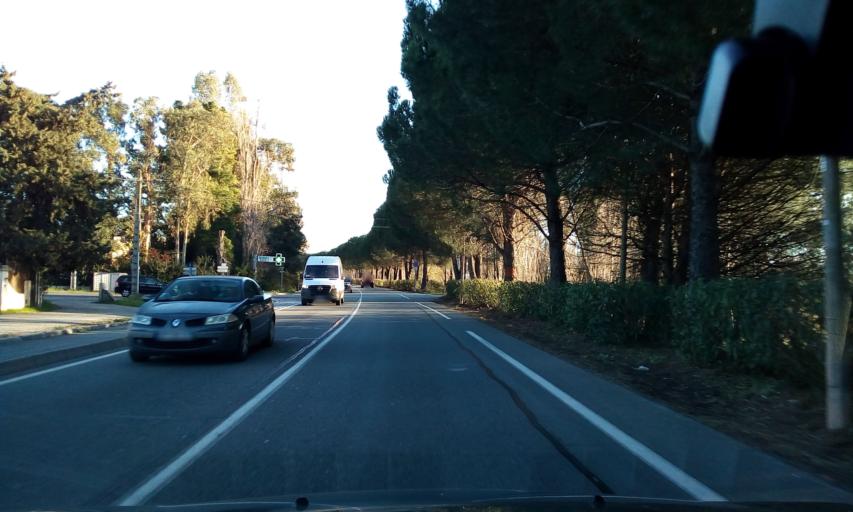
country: FR
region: Provence-Alpes-Cote d'Azur
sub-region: Departement du Var
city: Frejus
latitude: 43.4287
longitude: 6.7257
